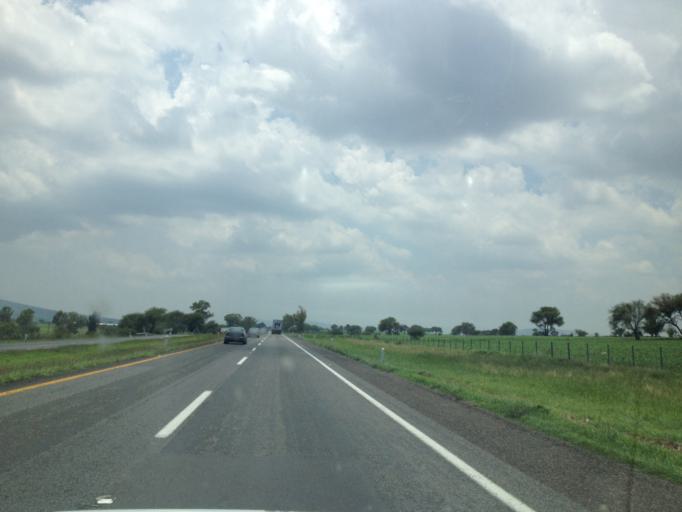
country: MX
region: Jalisco
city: La Barca
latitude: 20.3409
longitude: -102.6096
